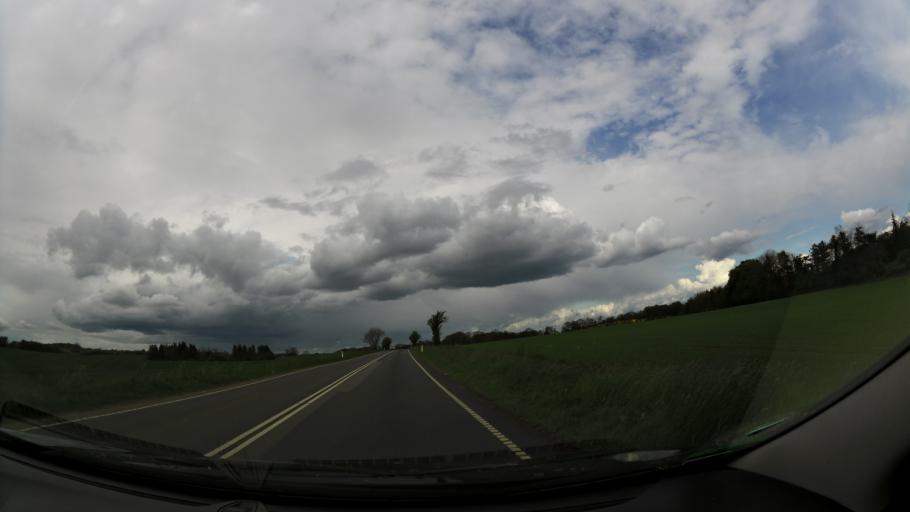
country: DK
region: South Denmark
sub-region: Svendborg Kommune
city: Thuro By
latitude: 55.1399
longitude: 10.7329
